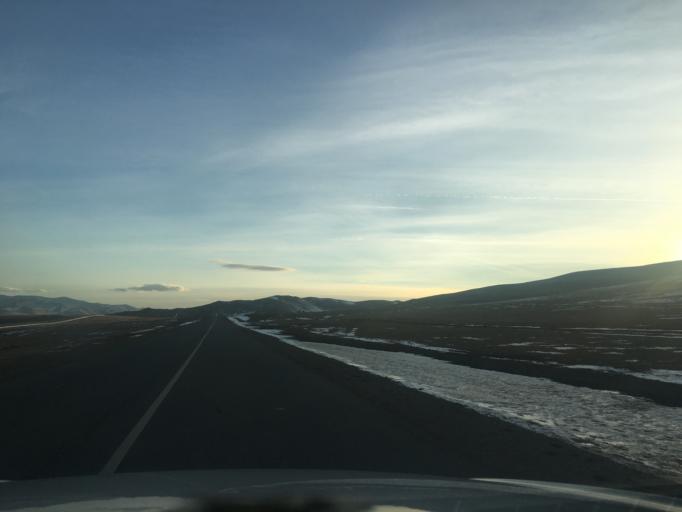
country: MN
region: Central Aimak
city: Mandal
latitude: 48.2215
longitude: 106.7134
